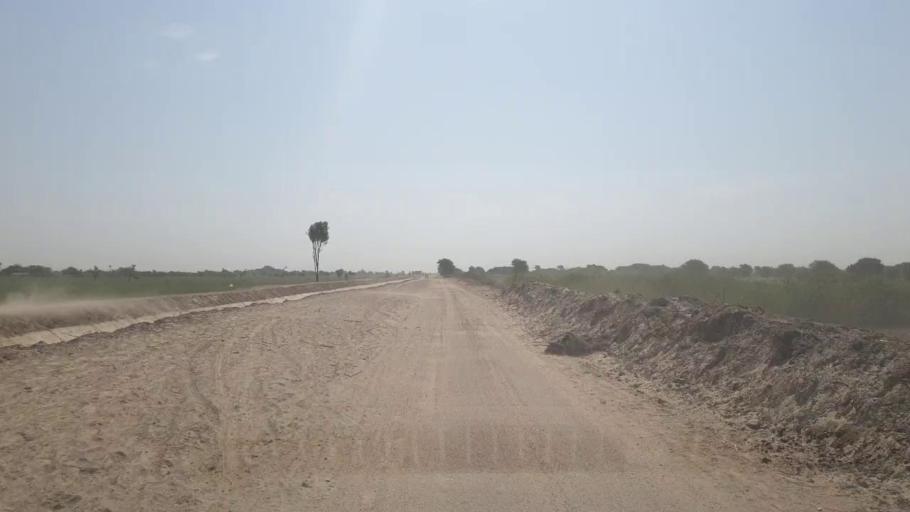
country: PK
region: Sindh
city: Kunri
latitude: 25.2691
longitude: 69.6273
